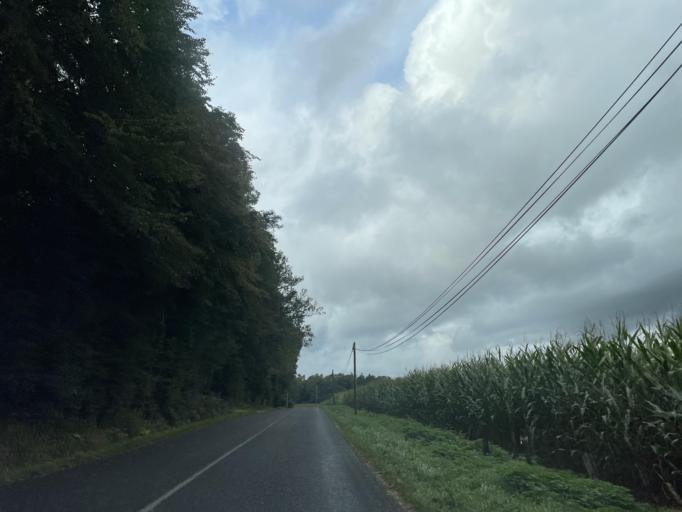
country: FR
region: Ile-de-France
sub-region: Departement de Seine-et-Marne
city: Saint-Jean-les-Deux-Jumeaux
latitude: 48.9093
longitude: 3.0217
